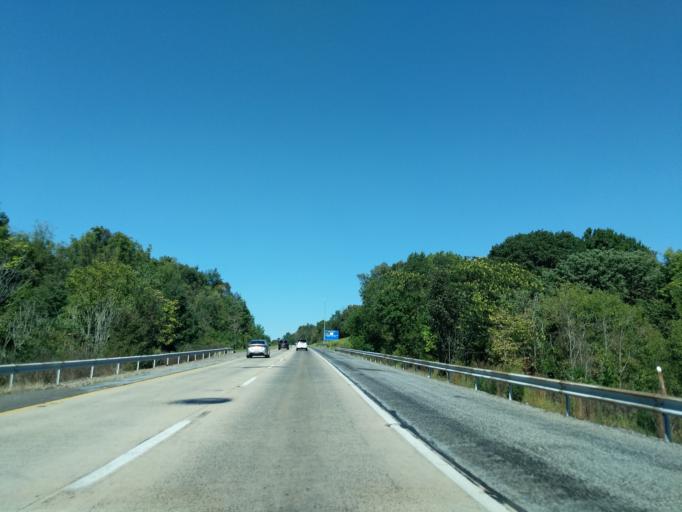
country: US
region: Pennsylvania
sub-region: Montgomery County
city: Audubon
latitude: 40.1483
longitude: -75.4576
